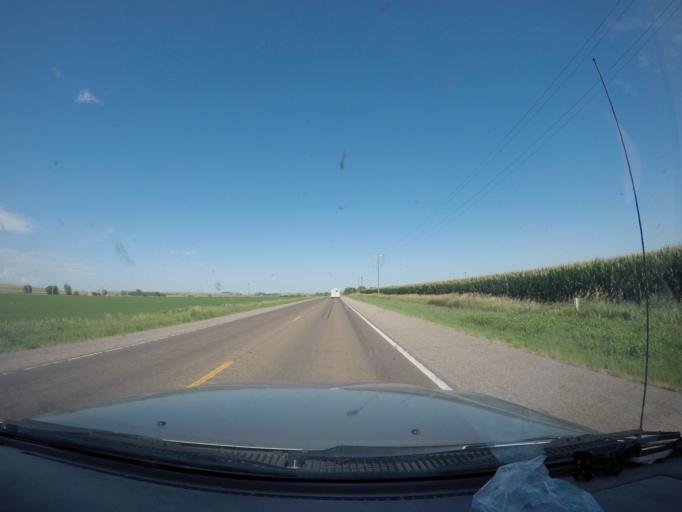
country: US
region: Nebraska
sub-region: Buffalo County
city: Kearney
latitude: 40.6997
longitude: -99.2196
